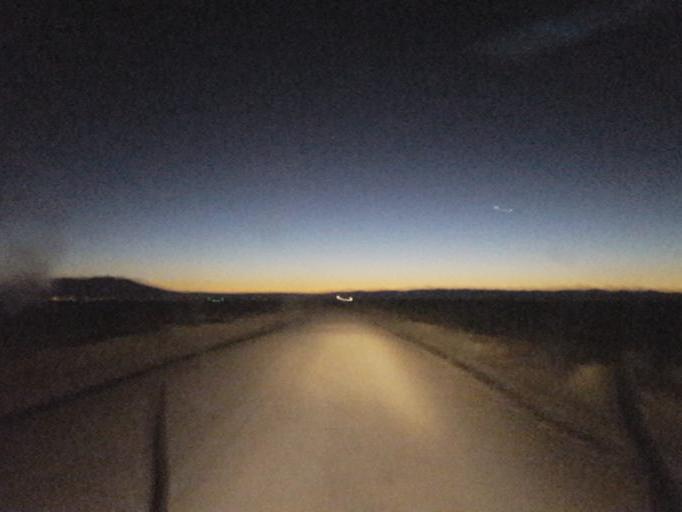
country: US
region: Colorado
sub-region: Rio Grande County
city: Monte Vista
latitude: 37.4011
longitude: -106.1182
